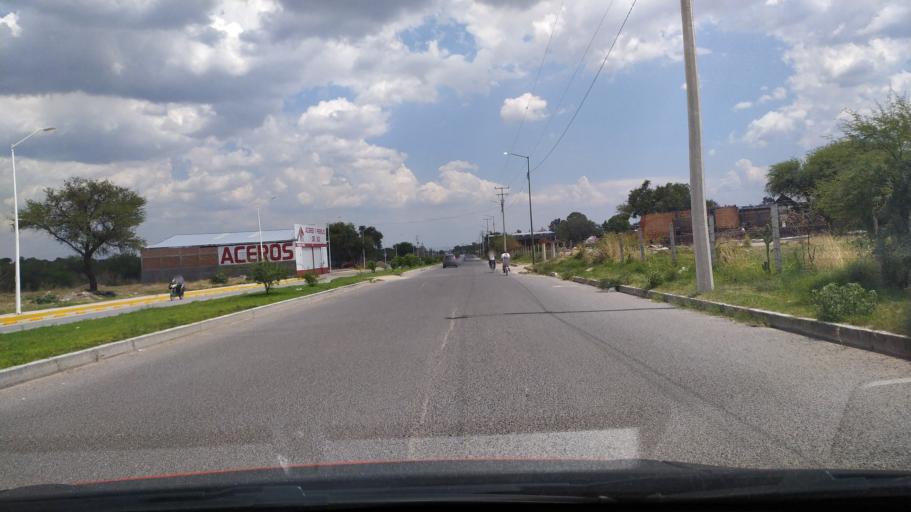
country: MX
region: Guanajuato
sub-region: Purisima del Rincon
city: Potrerillos (Guanajal)
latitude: 21.0503
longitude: -101.8691
